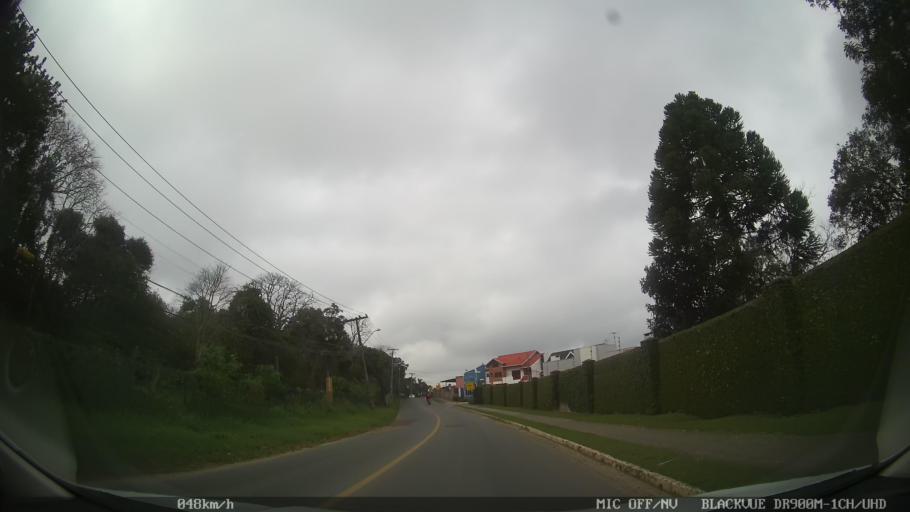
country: BR
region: Parana
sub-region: Almirante Tamandare
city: Almirante Tamandare
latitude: -25.3604
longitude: -49.2722
